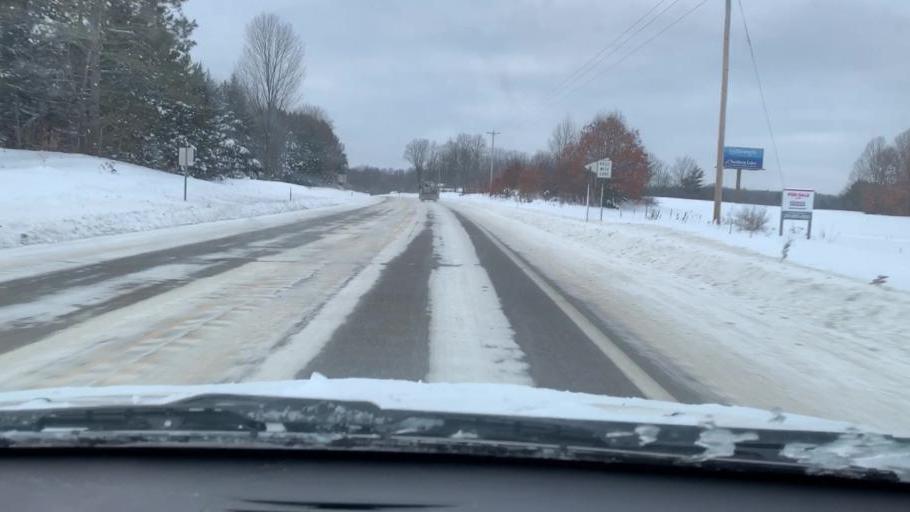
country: US
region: Michigan
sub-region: Wexford County
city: Manton
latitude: 44.5854
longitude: -85.3546
